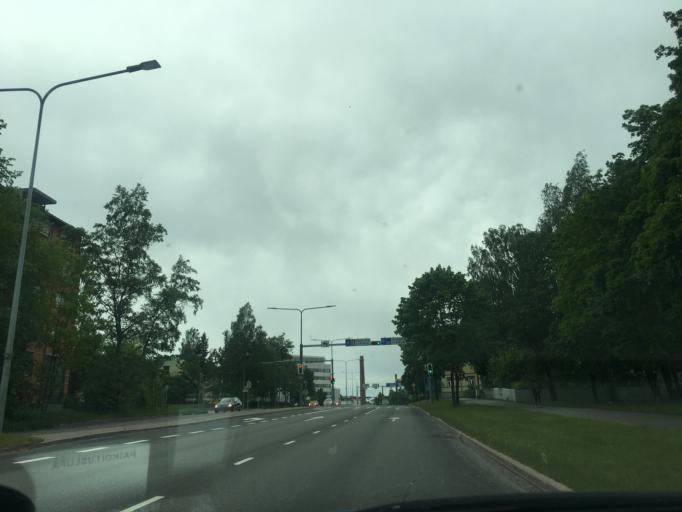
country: FI
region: Varsinais-Suomi
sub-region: Turku
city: Turku
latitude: 60.4566
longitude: 22.3012
